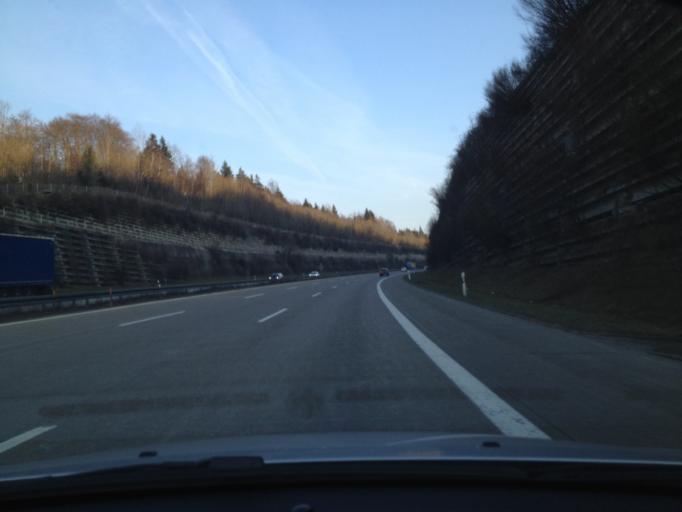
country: DE
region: Baden-Wuerttemberg
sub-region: Regierungsbezirk Stuttgart
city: Westhausen
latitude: 48.8637
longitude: 10.1896
